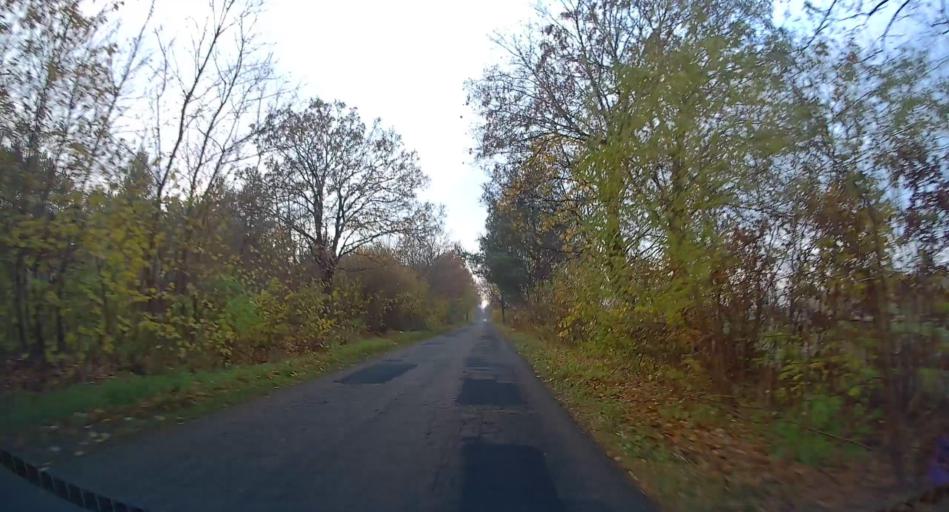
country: PL
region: Masovian Voivodeship
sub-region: Powiat zyrardowski
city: Puszcza Marianska
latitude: 51.9392
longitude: 20.3678
